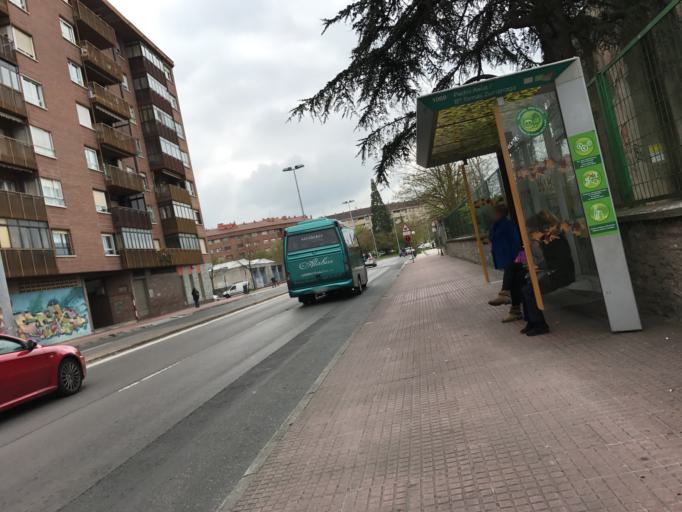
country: ES
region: Basque Country
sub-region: Provincia de Alava
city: Gasteiz / Vitoria
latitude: 42.8508
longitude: -2.6884
